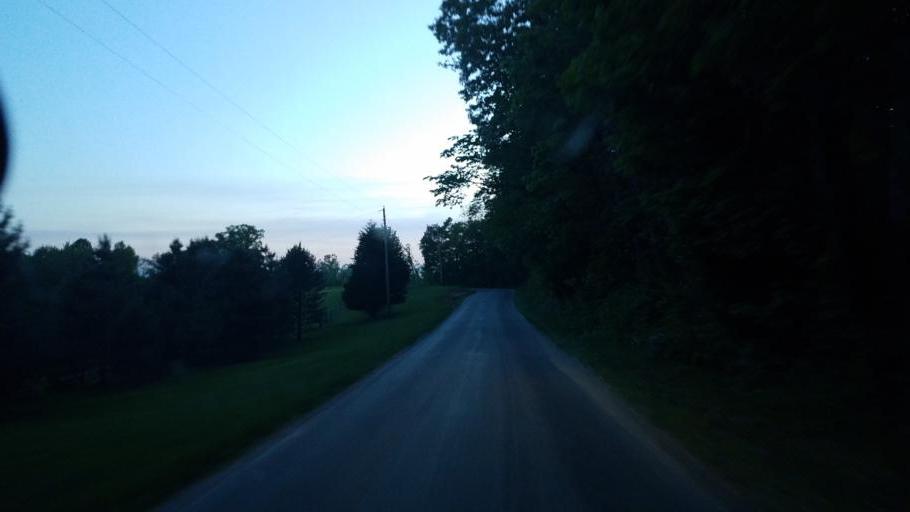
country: US
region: Ohio
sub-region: Highland County
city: Greenfield
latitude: 39.2046
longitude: -83.3759
